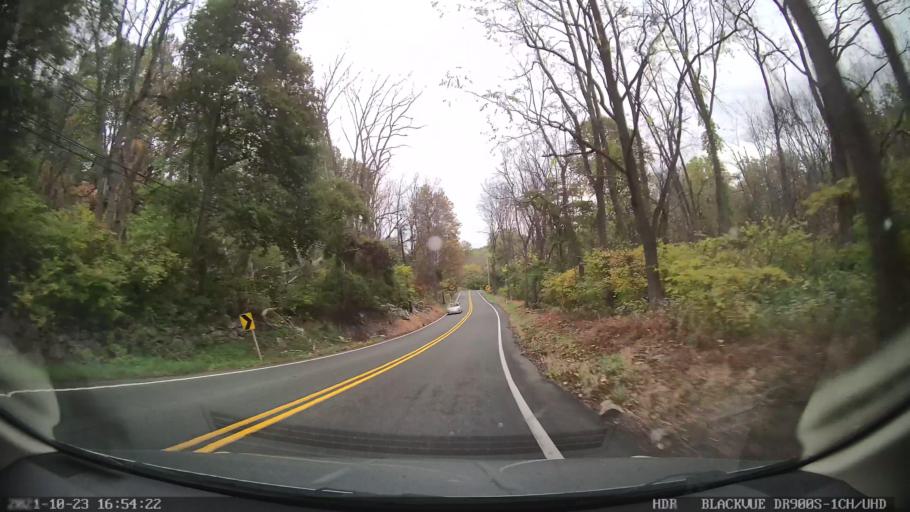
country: US
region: Pennsylvania
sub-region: Berks County
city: Red Lion
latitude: 40.4587
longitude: -75.5760
